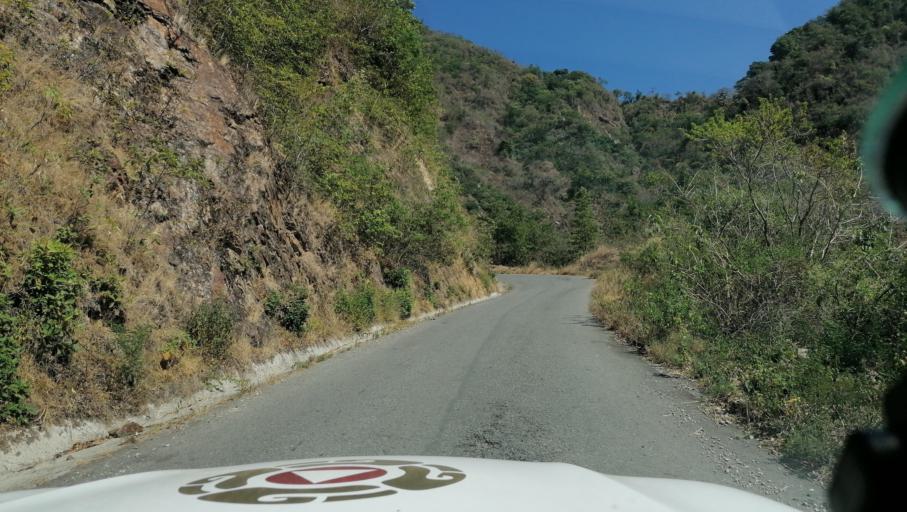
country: MX
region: Chiapas
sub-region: Cacahoatan
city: Benito Juarez
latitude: 15.1808
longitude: -92.1873
